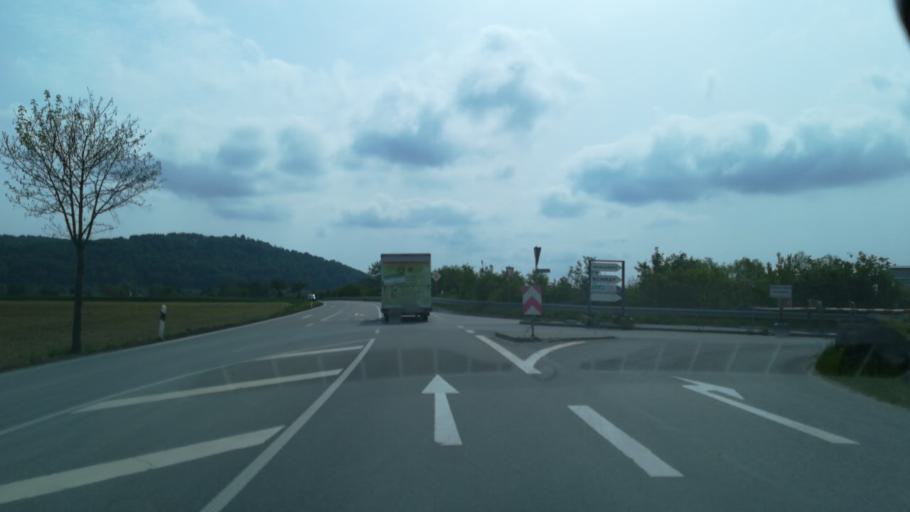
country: DE
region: Baden-Wuerttemberg
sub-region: Freiburg Region
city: Steisslingen
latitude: 47.7834
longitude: 8.9209
